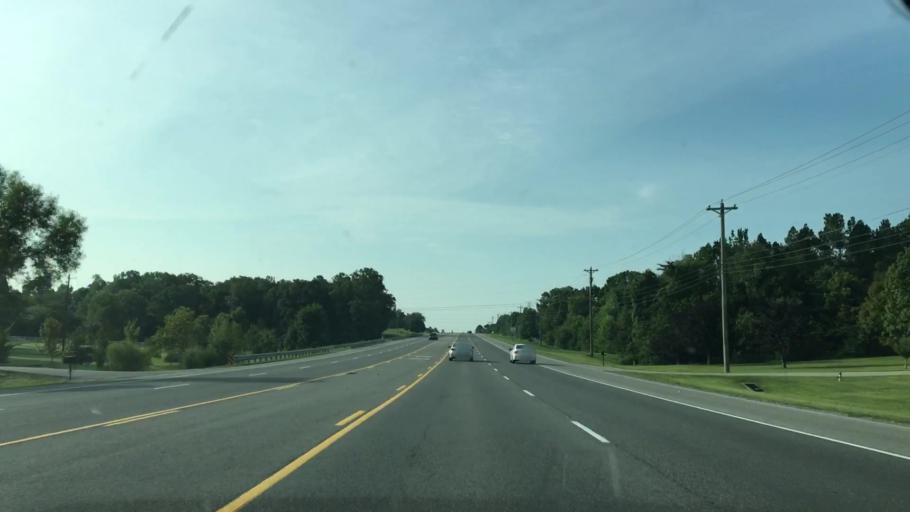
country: US
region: Tennessee
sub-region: Wilson County
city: Mount Juliet
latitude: 36.2166
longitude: -86.4229
